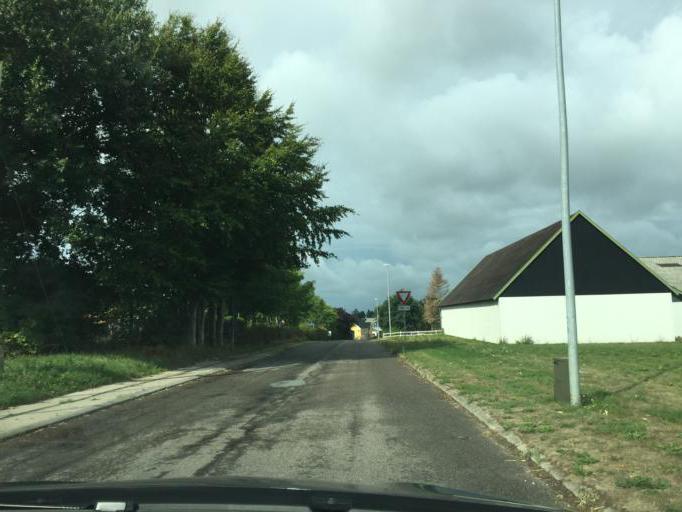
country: DK
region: South Denmark
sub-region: Assens Kommune
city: Harby
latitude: 55.2016
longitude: 10.1602
